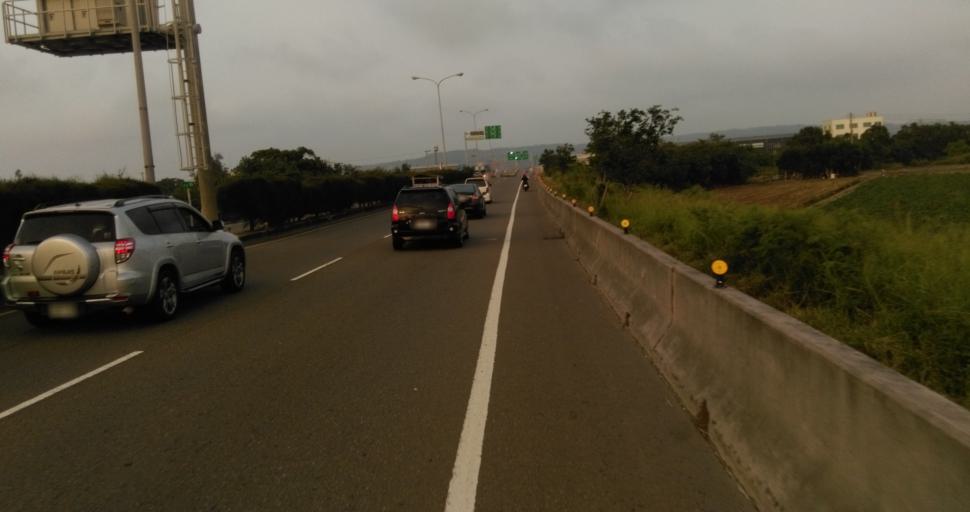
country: TW
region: Taiwan
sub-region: Hsinchu
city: Hsinchu
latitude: 24.8534
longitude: 120.9442
